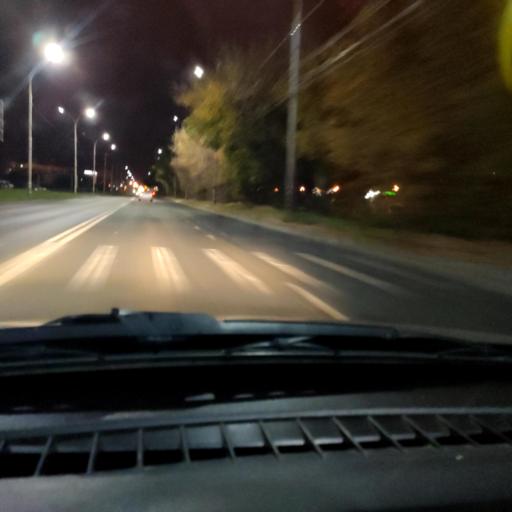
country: RU
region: Samara
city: Tol'yatti
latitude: 53.5485
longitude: 49.3173
